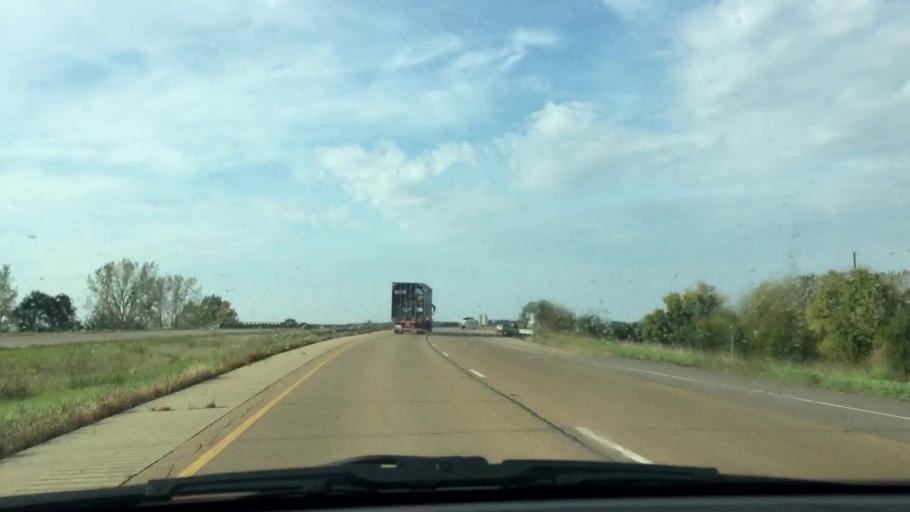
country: US
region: Illinois
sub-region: Whiteside County
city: Rock Falls
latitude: 41.7540
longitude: -89.6424
